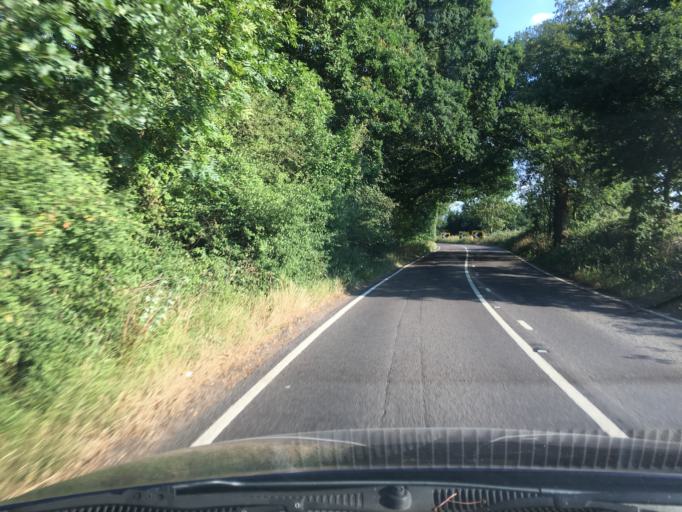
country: GB
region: England
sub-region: Bracknell Forest
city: Crowthorne
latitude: 51.3943
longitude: -0.7968
